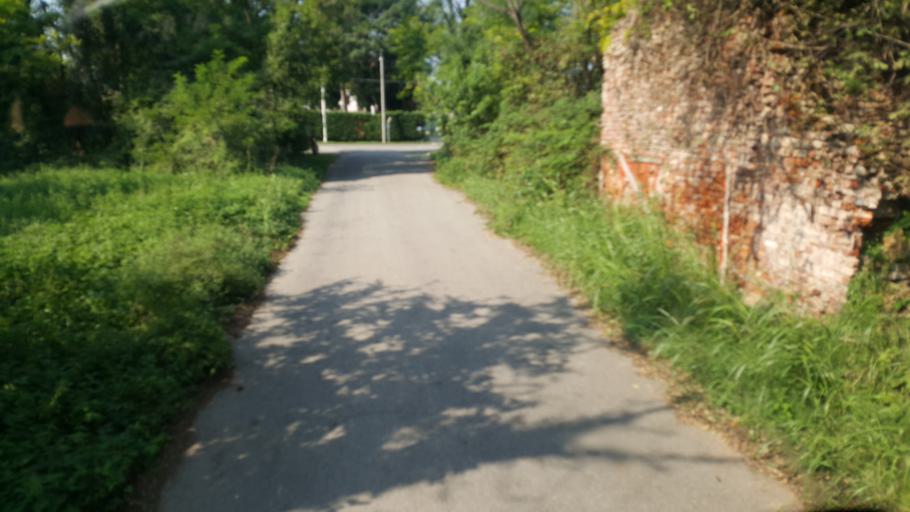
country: IT
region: Lombardy
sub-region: Provincia di Como
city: Locate Varesino
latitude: 45.6751
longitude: 8.9232
